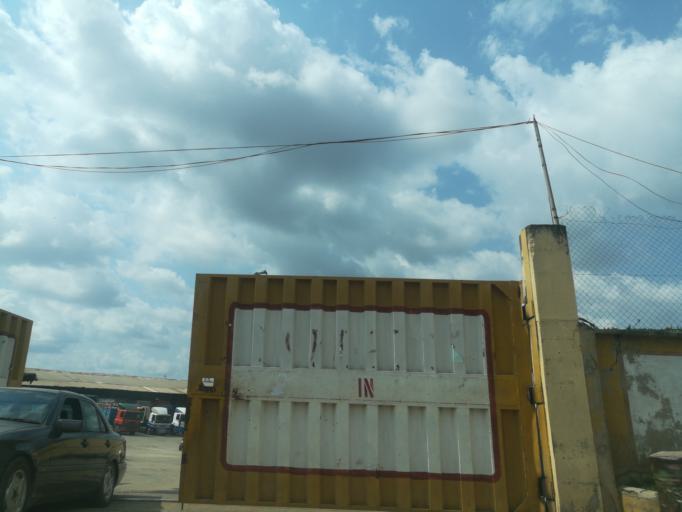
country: NG
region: Oyo
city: Ibadan
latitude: 7.3568
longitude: 3.8479
